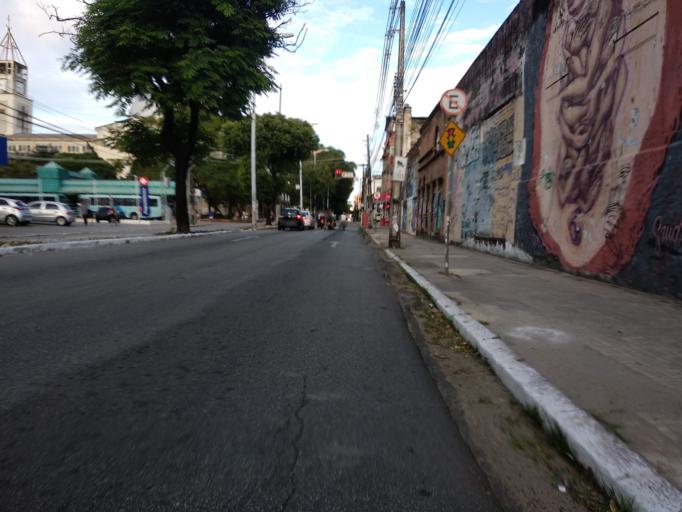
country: BR
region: Ceara
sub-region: Fortaleza
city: Fortaleza
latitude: -3.7325
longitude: -38.5279
